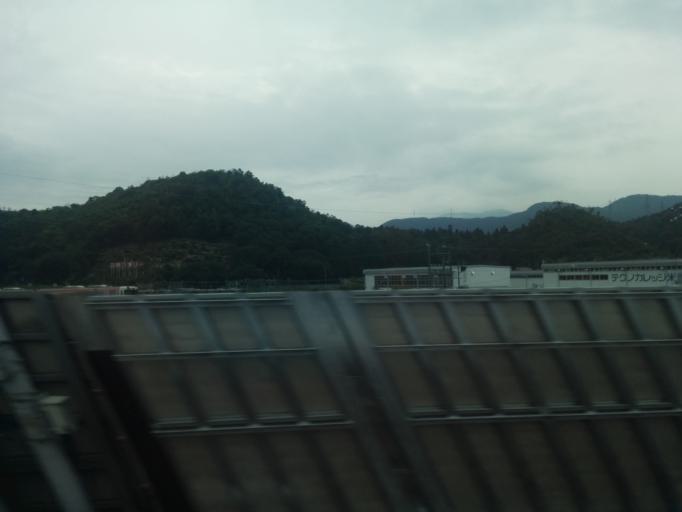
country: JP
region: Shiga Prefecture
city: Nagahama
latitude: 35.3230
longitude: 136.2916
